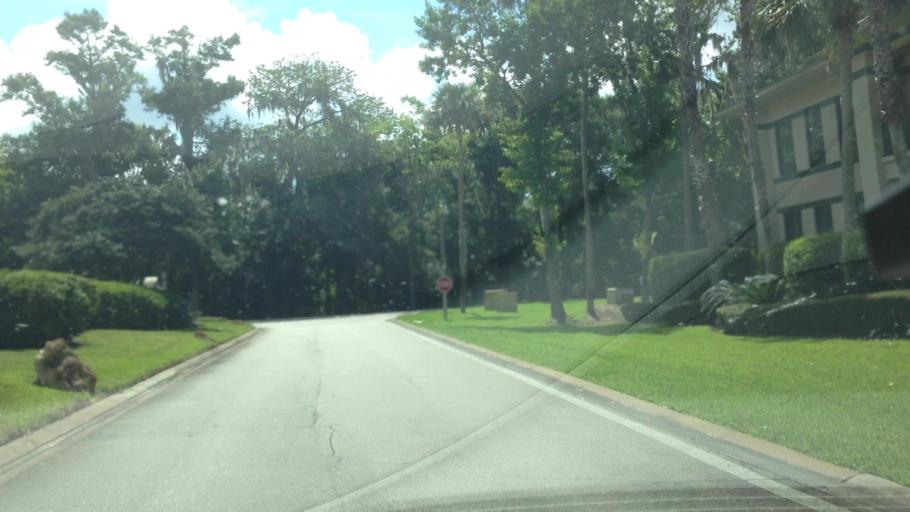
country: US
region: Florida
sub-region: Saint Johns County
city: Ponte Vedra Beach
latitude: 30.2537
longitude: -81.4012
